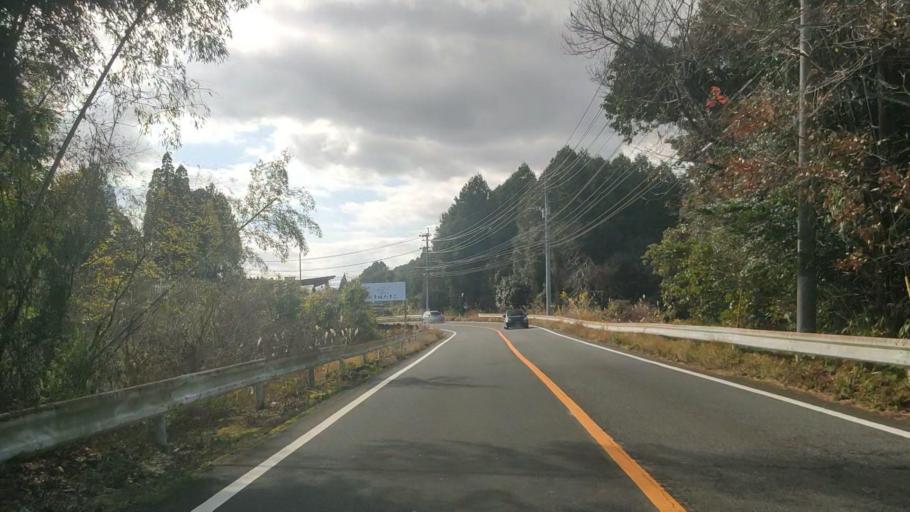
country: JP
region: Kagoshima
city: Okuchi-shinohara
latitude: 31.9273
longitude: 130.7021
